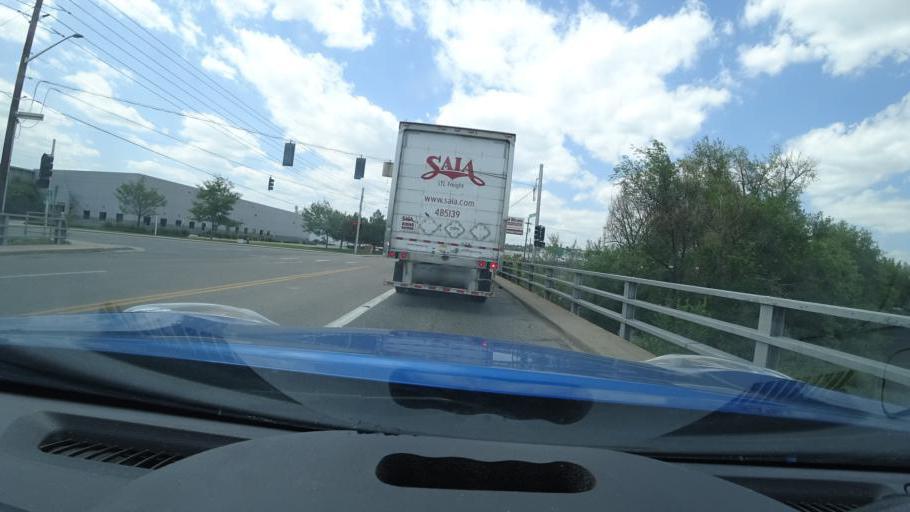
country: US
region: Colorado
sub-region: Arapahoe County
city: Englewood
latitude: 39.6605
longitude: -105.0039
